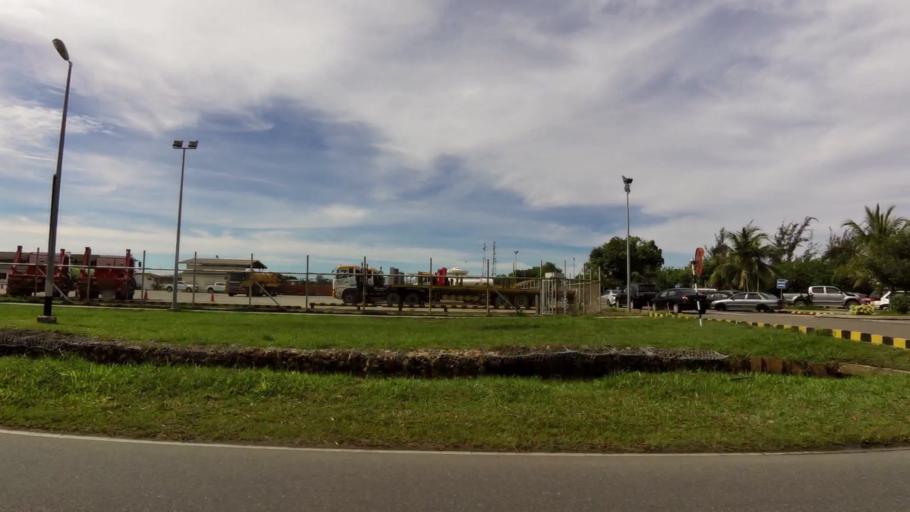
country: BN
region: Belait
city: Seria
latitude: 4.6201
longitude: 114.3308
